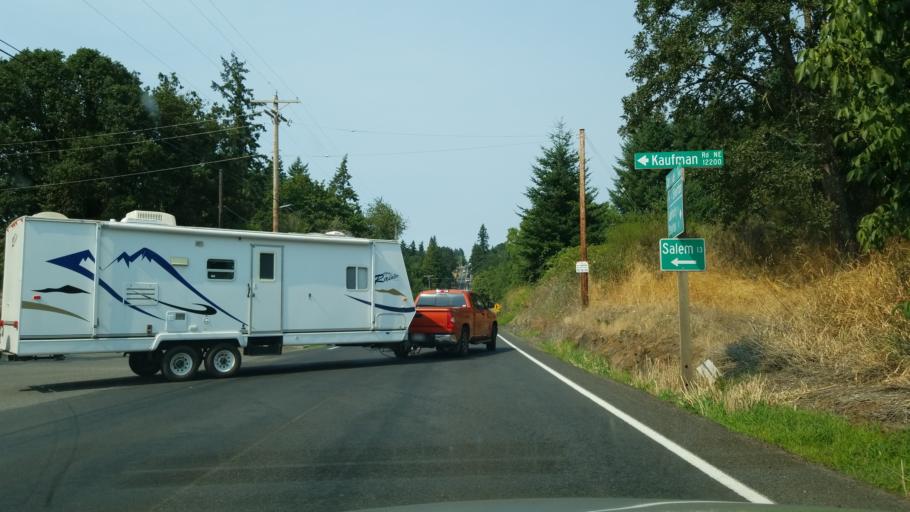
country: US
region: Oregon
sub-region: Marion County
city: Silverton
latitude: 44.9672
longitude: -122.8095
